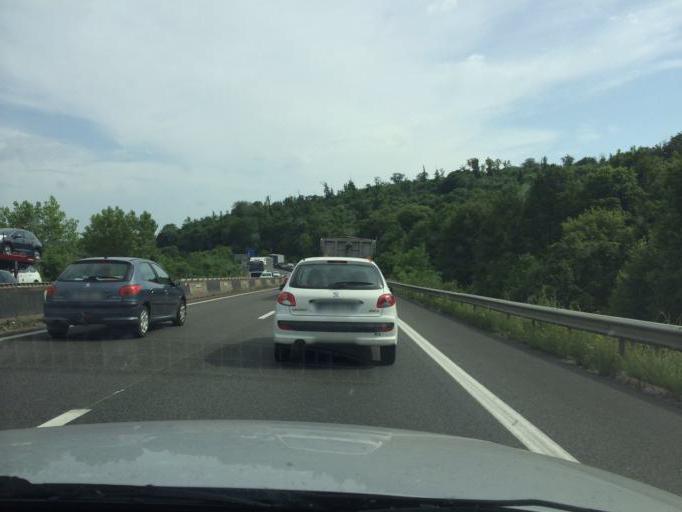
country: FR
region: Lorraine
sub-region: Departement de Meurthe-et-Moselle
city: Vandoeuvre-les-Nancy
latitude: 48.6389
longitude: 6.1709
